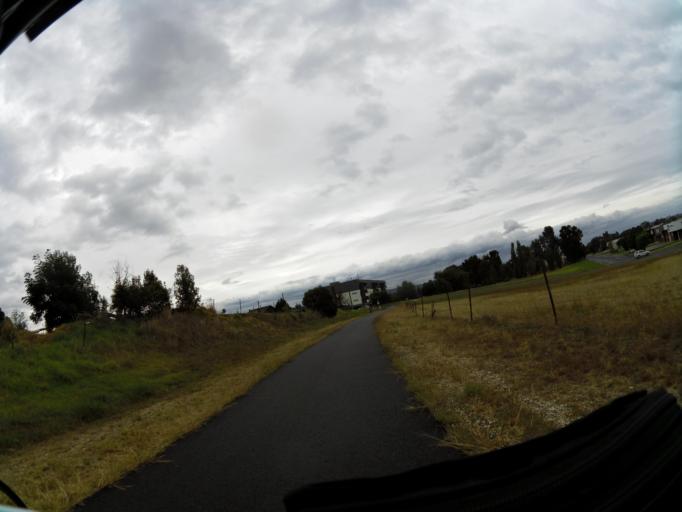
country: AU
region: Victoria
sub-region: Wodonga
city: Wodonga
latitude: -36.1236
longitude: 146.8929
